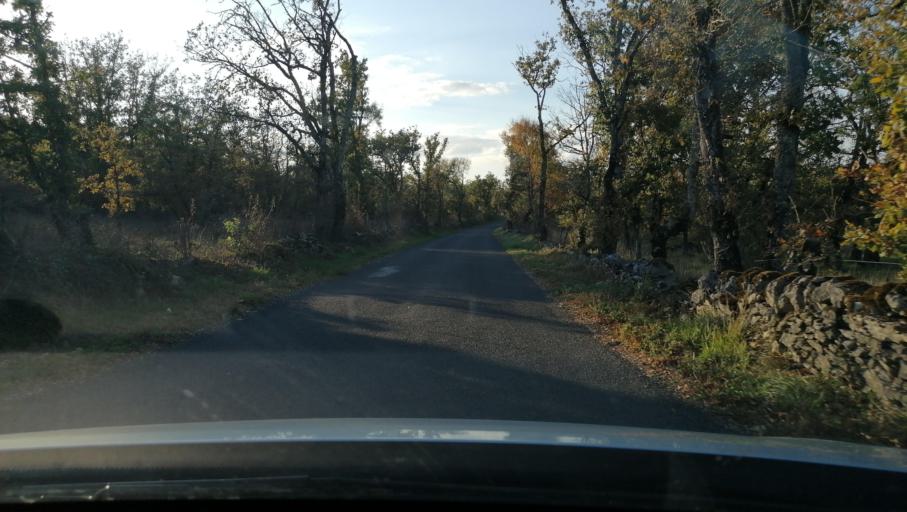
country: FR
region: Midi-Pyrenees
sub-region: Departement du Lot
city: Vayrac
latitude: 44.8695
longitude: 1.6589
